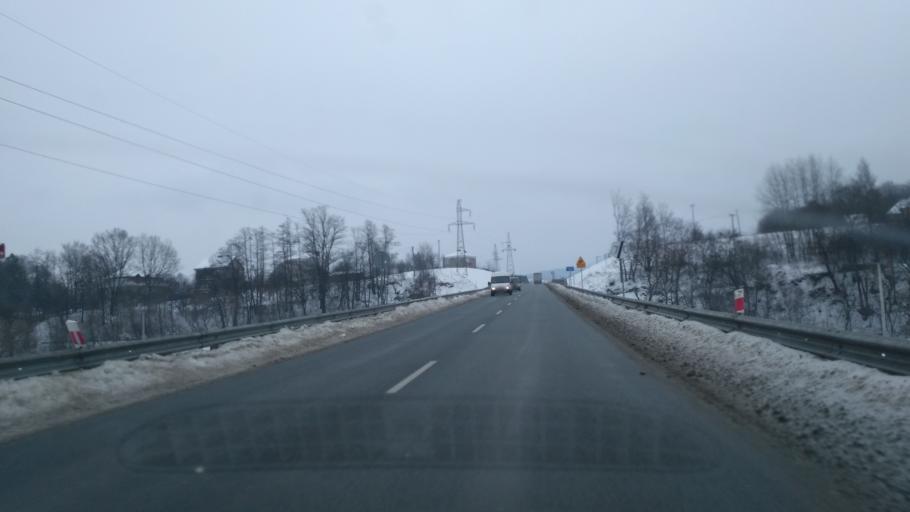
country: PL
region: Subcarpathian Voivodeship
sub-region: Powiat strzyzowski
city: Strzyzow
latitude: 49.8616
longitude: 21.7975
